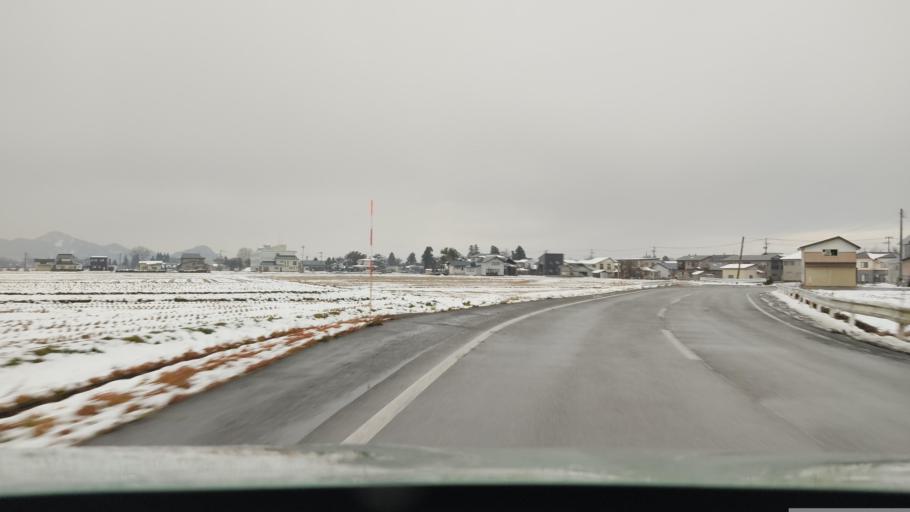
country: JP
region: Akita
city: Omagari
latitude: 39.4544
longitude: 140.5278
